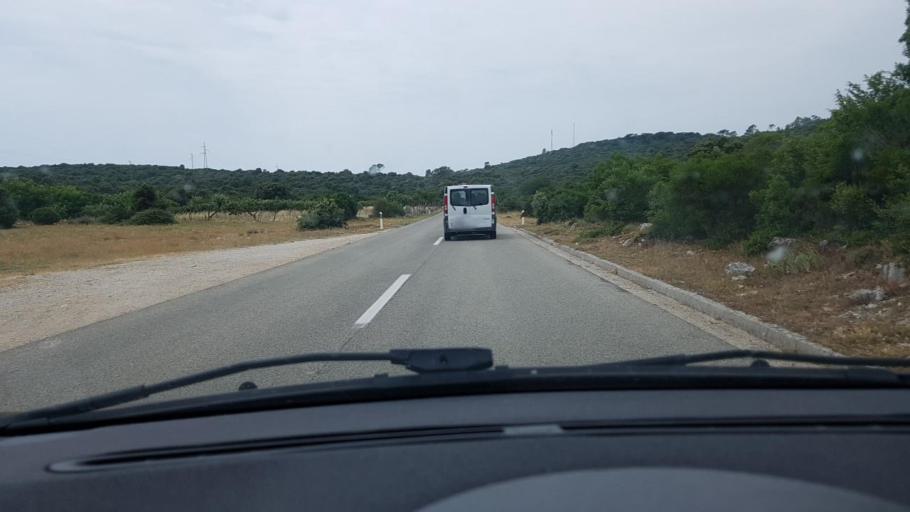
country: HR
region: Dubrovacko-Neretvanska
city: Smokvica
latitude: 42.9485
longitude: 16.9906
